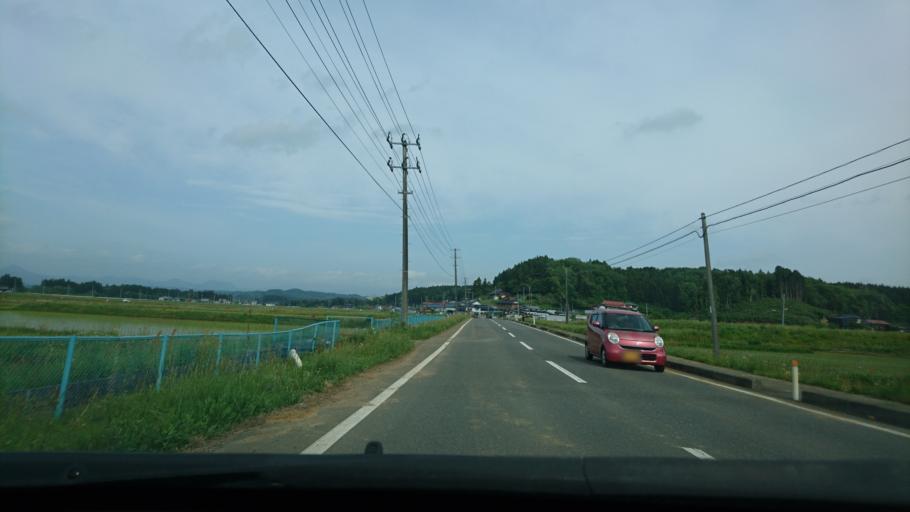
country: JP
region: Iwate
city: Ichinoseki
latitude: 38.8234
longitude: 141.0347
